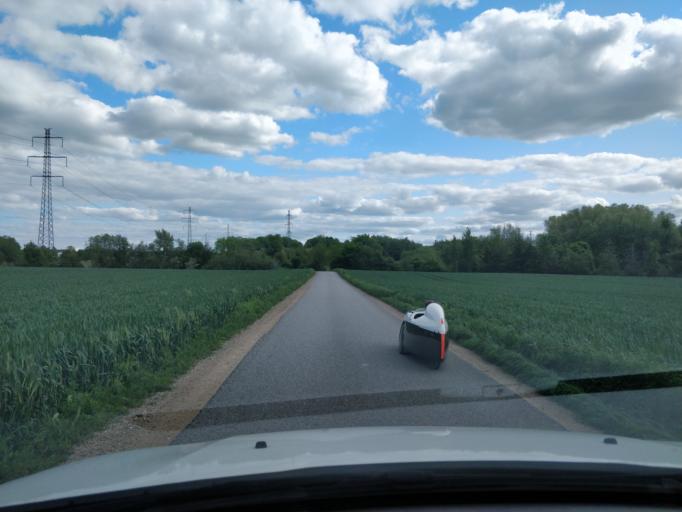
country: DK
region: Capital Region
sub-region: Hoje-Taastrup Kommune
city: Flong
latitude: 55.6824
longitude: 12.2194
